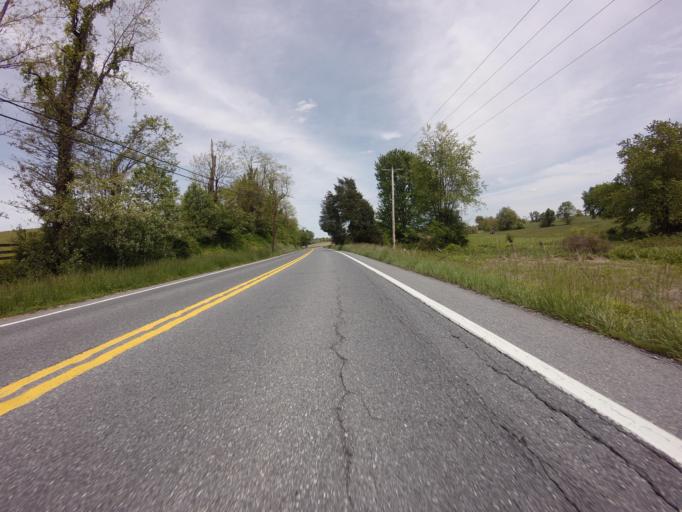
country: US
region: Maryland
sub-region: Frederick County
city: Linganore
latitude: 39.4948
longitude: -77.1900
